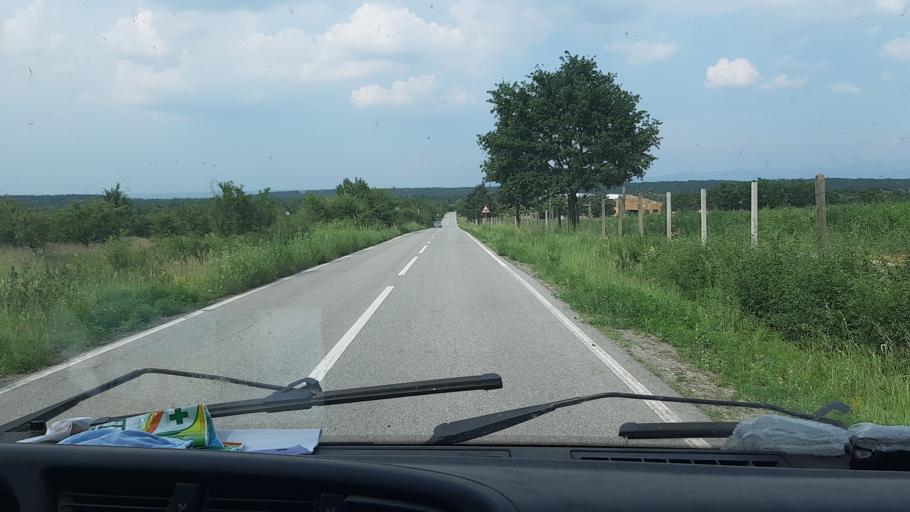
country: RO
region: Timis
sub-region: Comuna Victor Vlad Delamarina
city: Victor Vlad Delamarina
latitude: 45.5754
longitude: 21.8725
